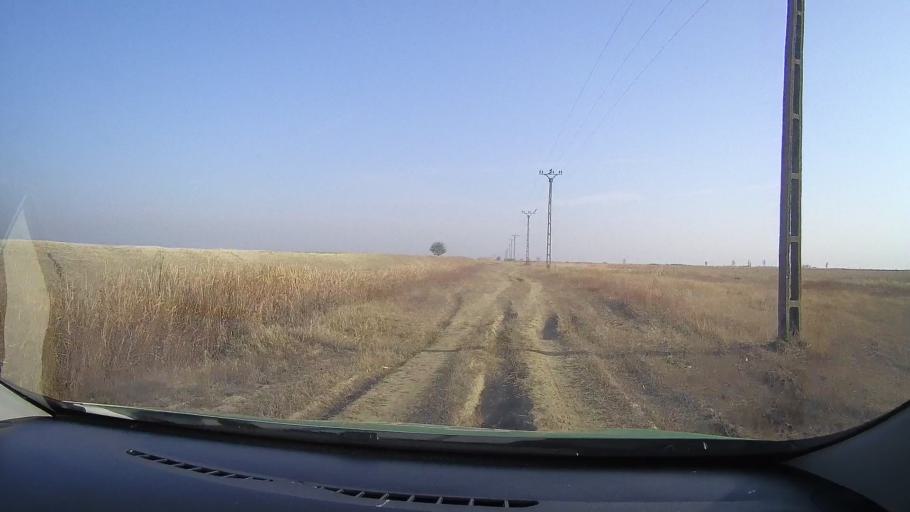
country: RO
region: Arad
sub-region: Comuna Pilu
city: Pilu
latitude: 46.5483
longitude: 21.3321
